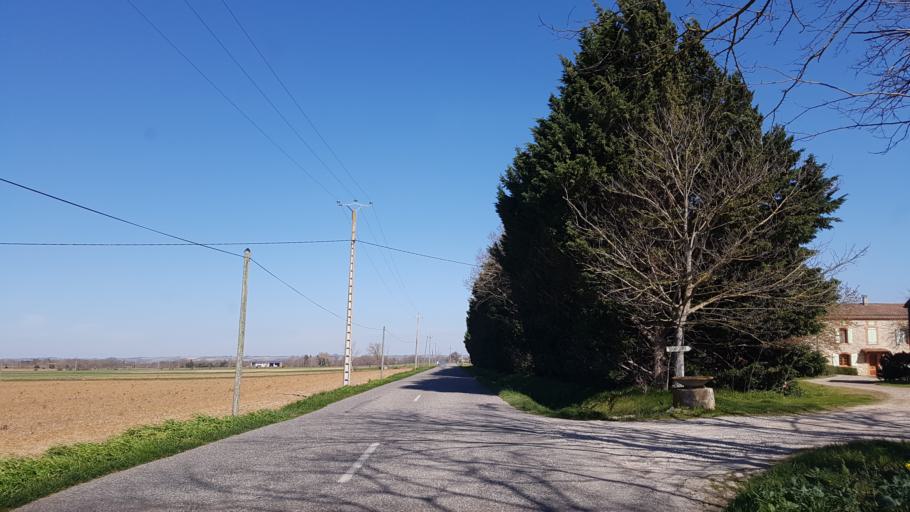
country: FR
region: Languedoc-Roussillon
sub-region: Departement de l'Aude
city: Belpech
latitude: 43.1772
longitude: 1.7109
